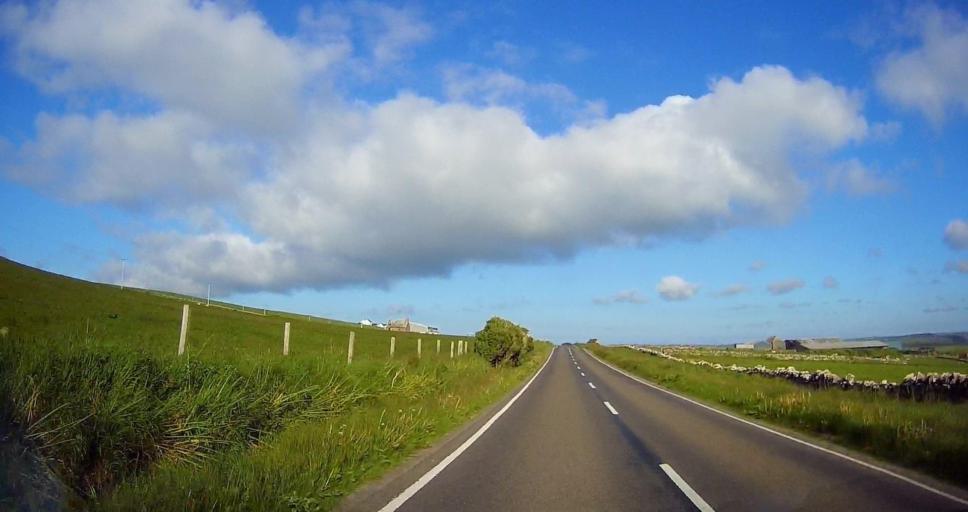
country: GB
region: Scotland
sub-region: Orkney Islands
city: Orkney
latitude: 58.9797
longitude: -3.0278
